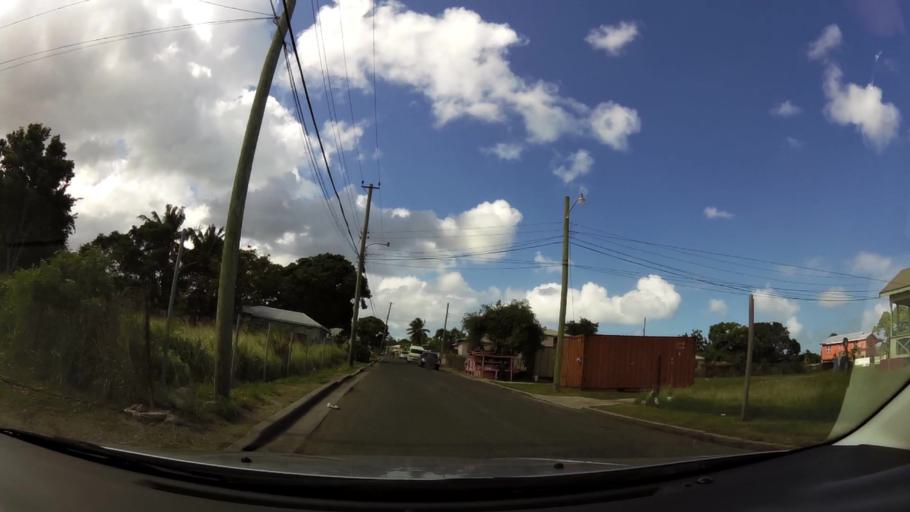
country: AG
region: Saint John
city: Saint John's
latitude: 17.1063
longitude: -61.8399
